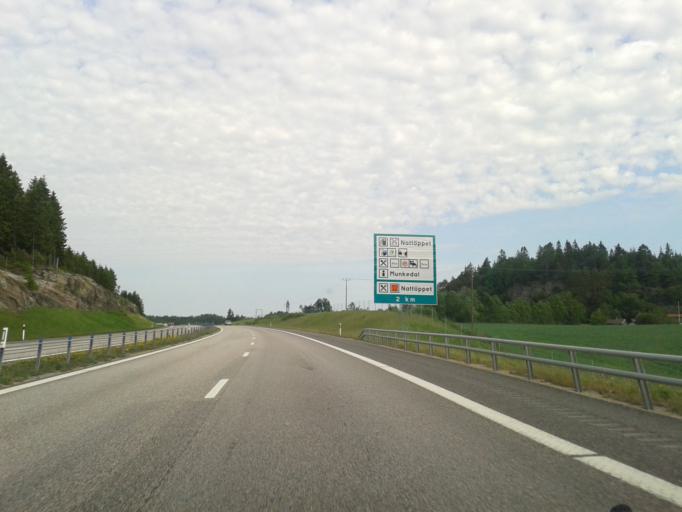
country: SE
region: Vaestra Goetaland
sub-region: Munkedals Kommun
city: Munkedal
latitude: 58.4731
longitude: 11.6462
